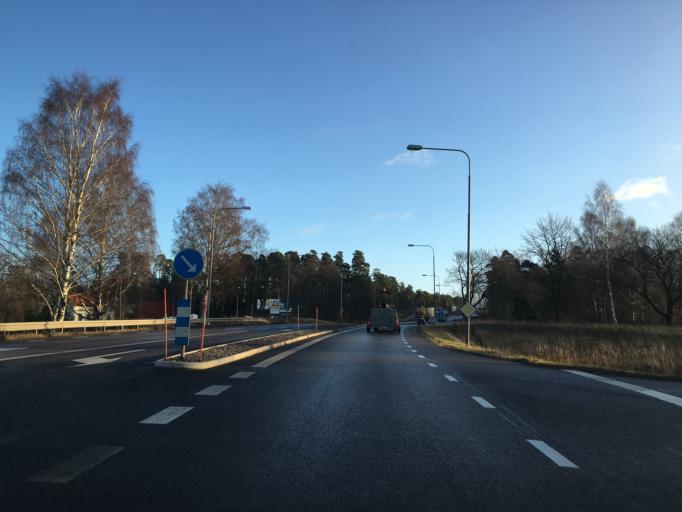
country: SE
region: Kalmar
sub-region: Vasterviks Kommun
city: Vaestervik
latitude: 57.7686
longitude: 16.5763
